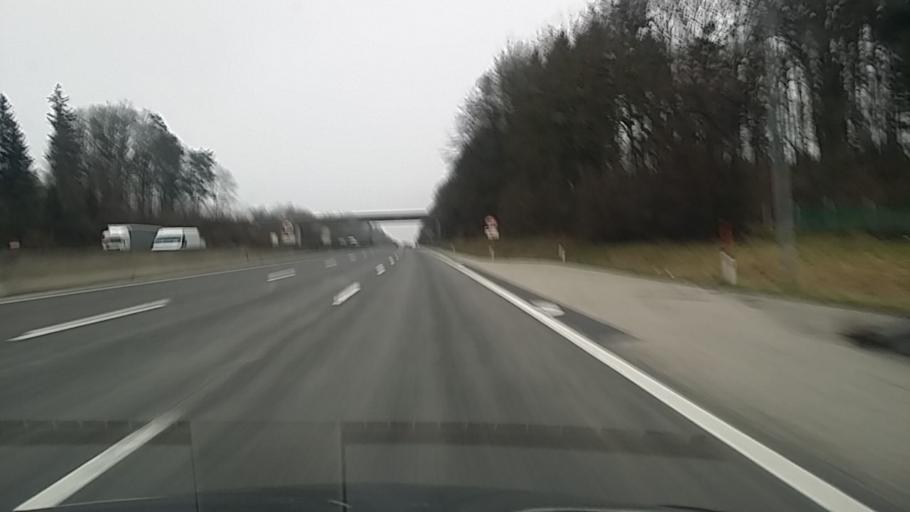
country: AT
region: Lower Austria
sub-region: Politischer Bezirk Amstetten
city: Sankt Valentin
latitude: 48.1644
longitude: 14.5522
